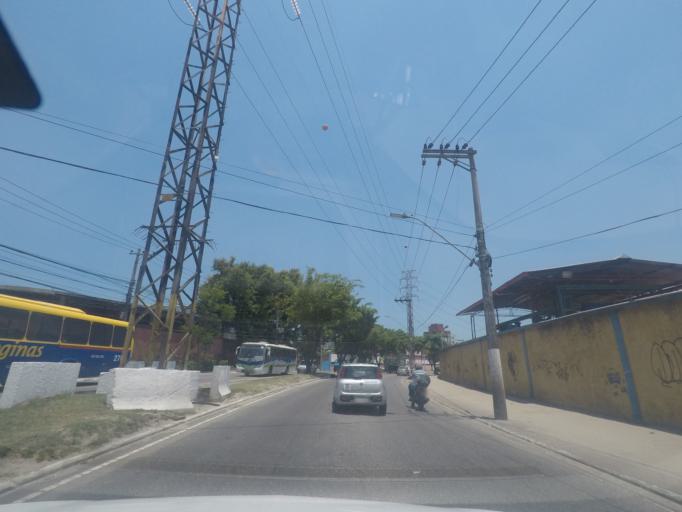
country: BR
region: Rio de Janeiro
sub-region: Duque De Caxias
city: Duque de Caxias
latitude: -22.7943
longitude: -43.3062
